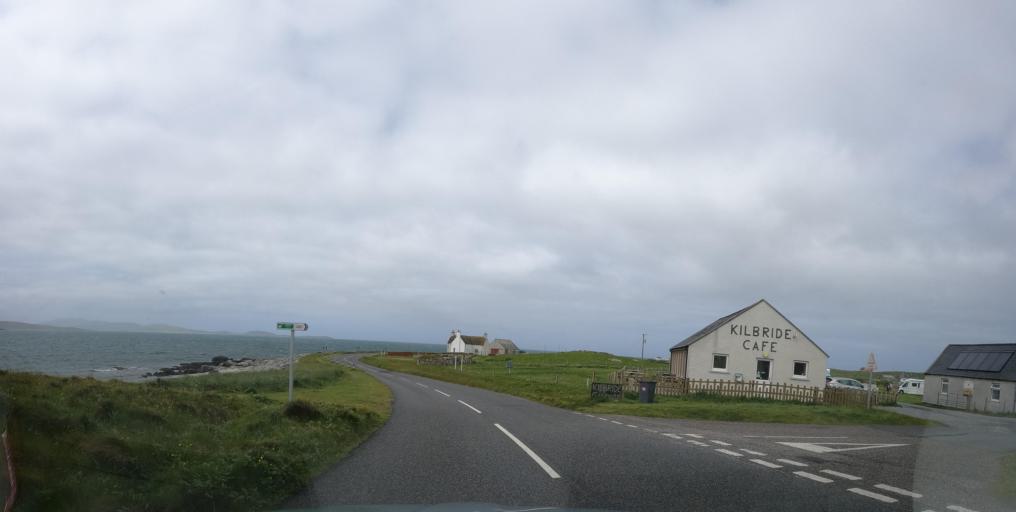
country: GB
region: Scotland
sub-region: Eilean Siar
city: Isle of South Uist
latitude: 57.1031
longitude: -7.3562
